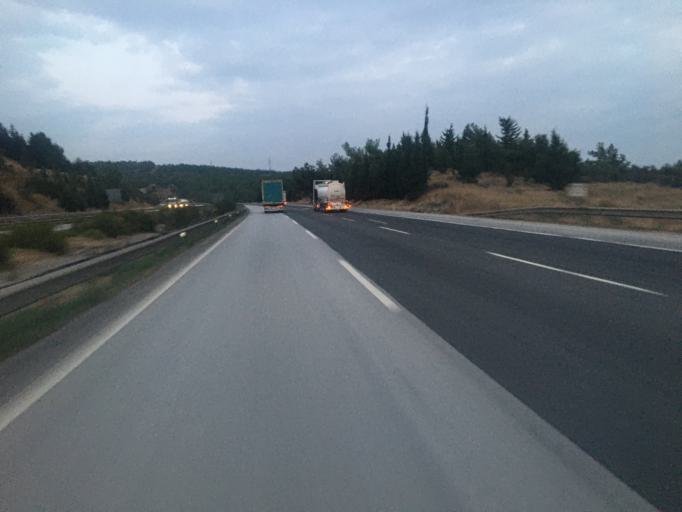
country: TR
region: Osmaniye
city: Haruniye
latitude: 37.1733
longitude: 36.3702
